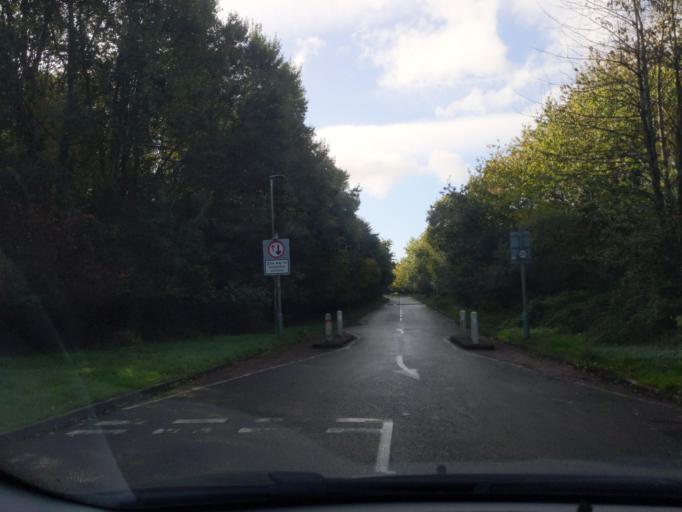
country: GB
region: England
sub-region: Devon
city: Plympton
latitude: 50.4062
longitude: -4.0983
